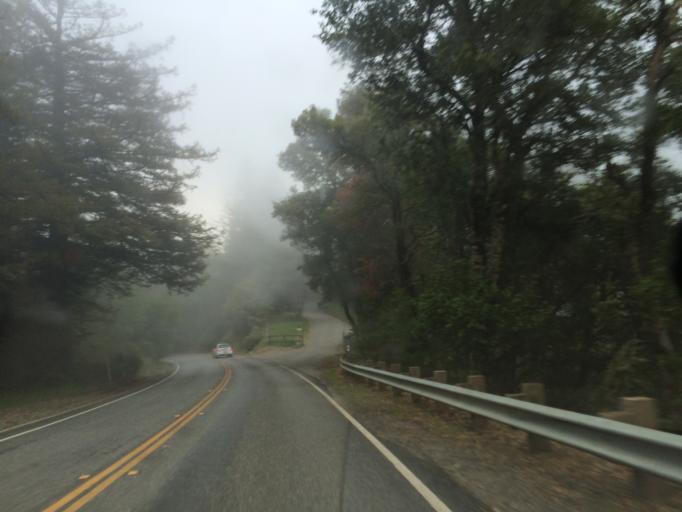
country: US
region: California
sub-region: Santa Clara County
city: Los Altos Hills
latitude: 37.3148
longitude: -122.1870
